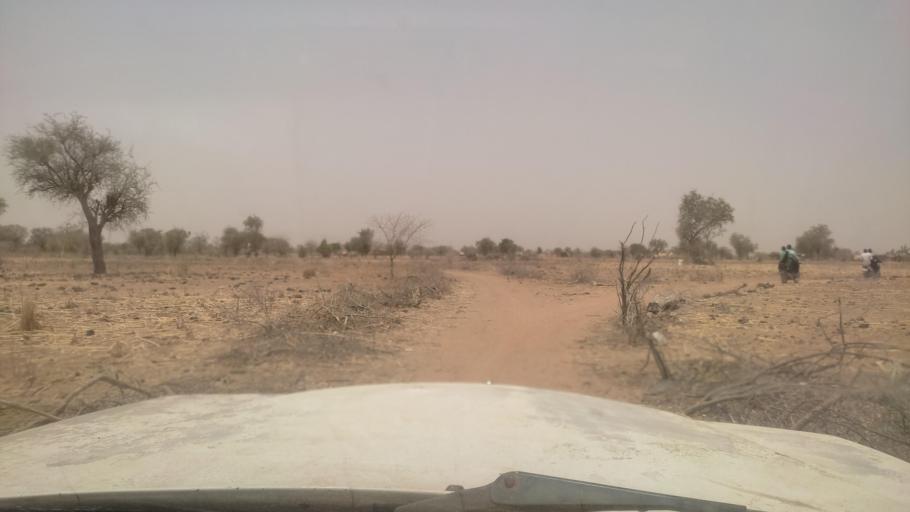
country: BF
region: Est
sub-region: Gnagna Province
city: Bogande
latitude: 13.0404
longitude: -0.0698
